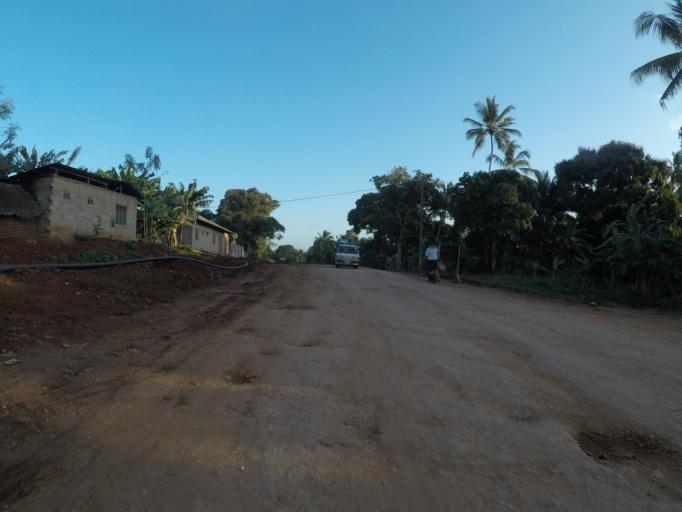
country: TZ
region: Zanzibar North
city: Gamba
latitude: -5.9160
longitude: 39.2992
